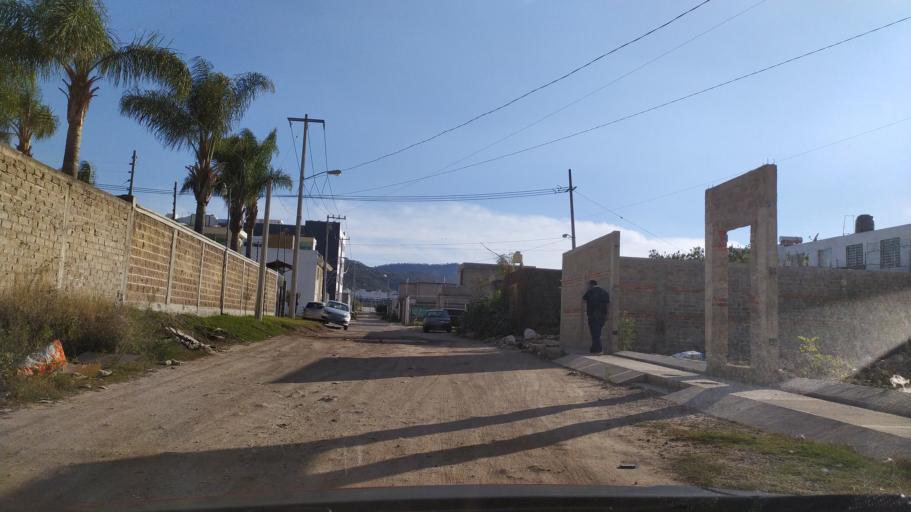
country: MX
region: Jalisco
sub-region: Tlajomulco de Zuniga
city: Palomar
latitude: 20.6306
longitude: -103.4753
